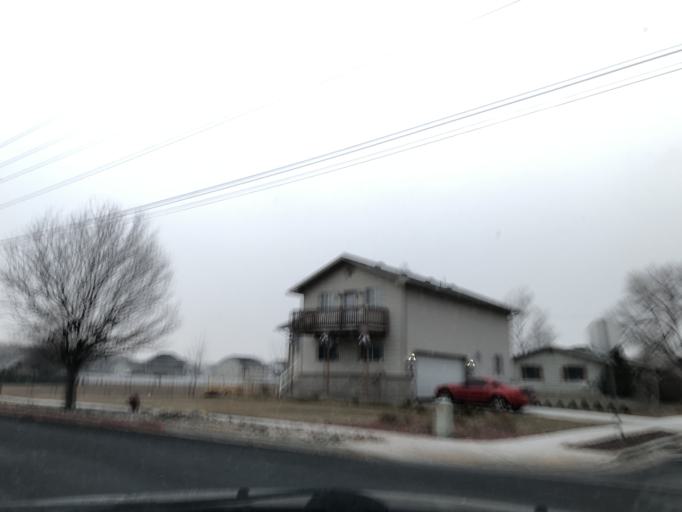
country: US
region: Utah
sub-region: Cache County
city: Logan
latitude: 41.7133
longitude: -111.8528
